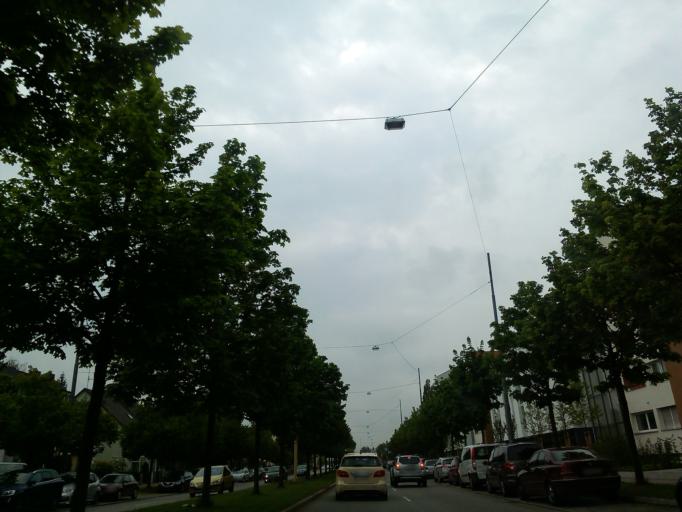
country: DE
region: Bavaria
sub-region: Upper Bavaria
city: Bogenhausen
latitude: 48.1257
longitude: 11.6475
